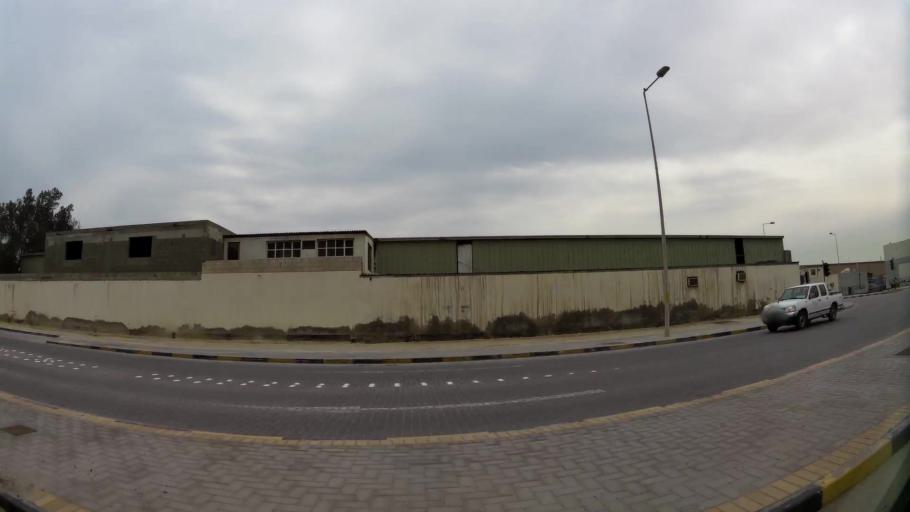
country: BH
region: Northern
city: Sitrah
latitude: 26.1778
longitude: 50.6038
